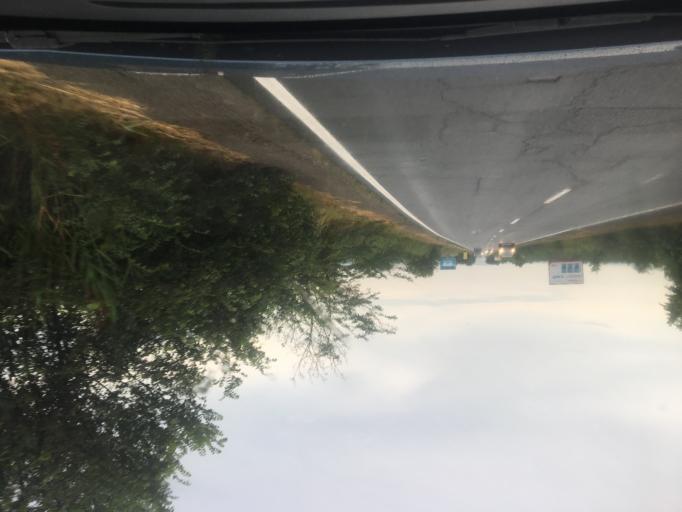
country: BG
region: Burgas
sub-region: Obshtina Pomorie
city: Pomorie
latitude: 42.5880
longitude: 27.6108
